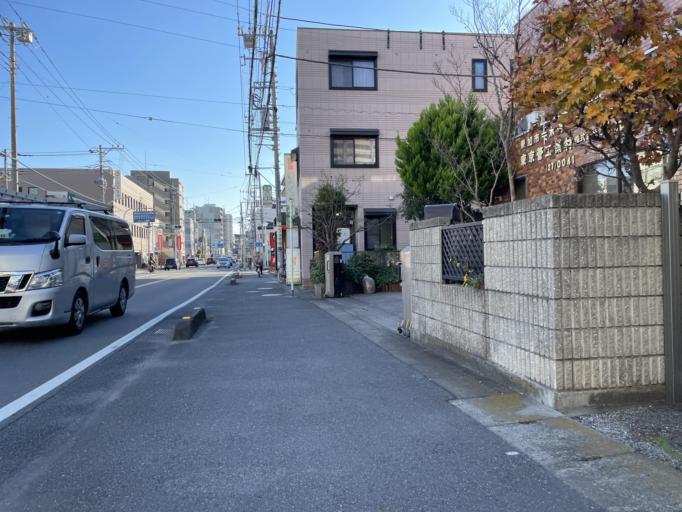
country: JP
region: Saitama
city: Soka
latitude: 35.8303
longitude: 139.8073
